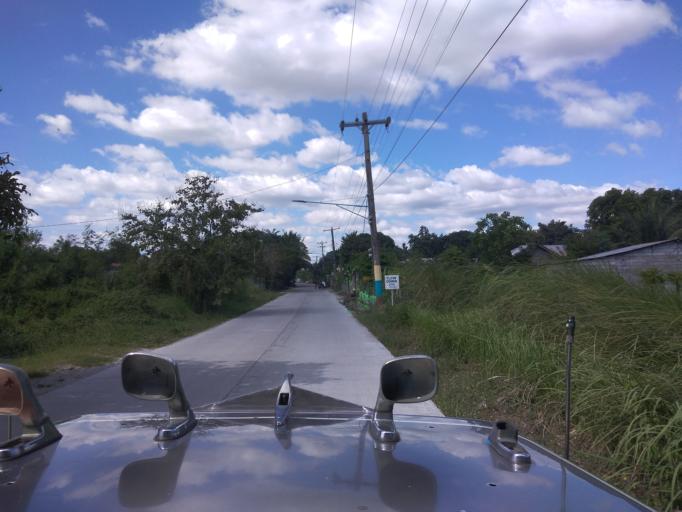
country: PH
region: Central Luzon
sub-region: Province of Pampanga
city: Magliman
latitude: 15.0264
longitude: 120.6365
